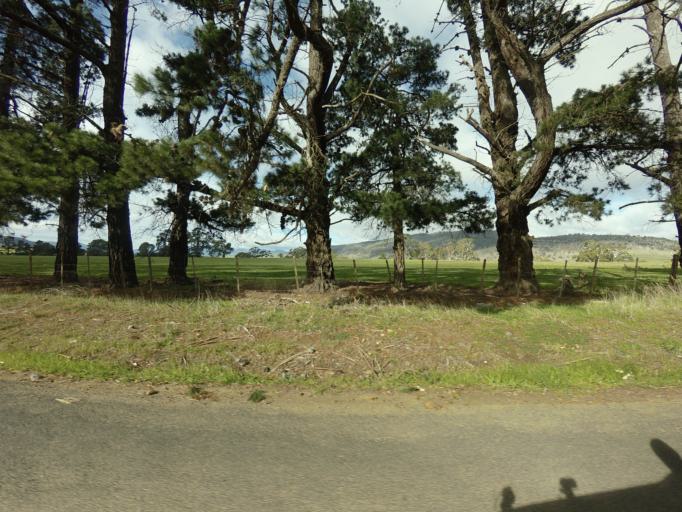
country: AU
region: Tasmania
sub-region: Derwent Valley
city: New Norfolk
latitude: -42.7119
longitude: 146.8924
